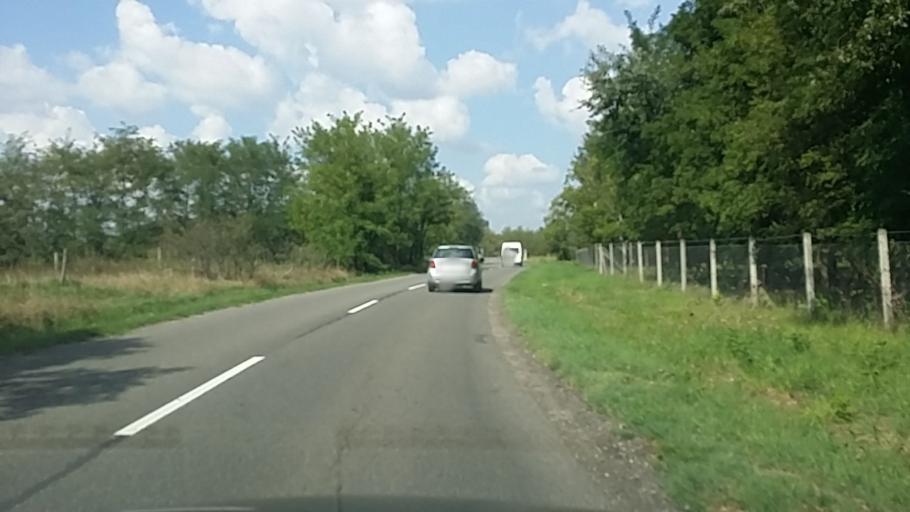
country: HU
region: Bacs-Kiskun
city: Tiszaalpar
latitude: 46.8311
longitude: 19.9744
